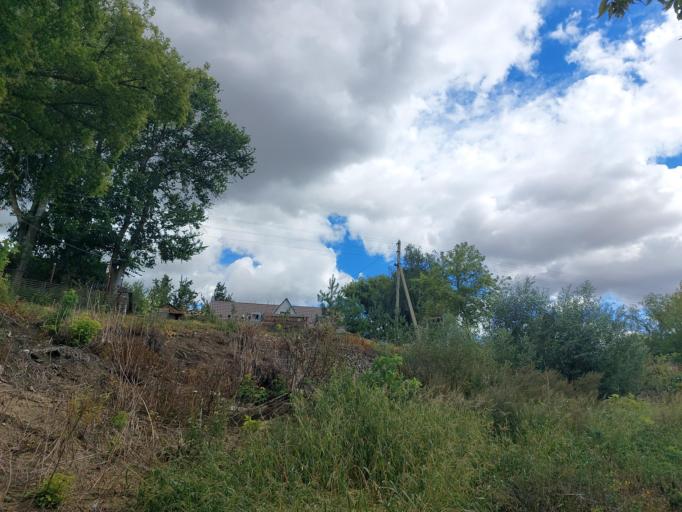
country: RU
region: Lipetsk
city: Terbuny
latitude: 52.2635
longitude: 38.2068
